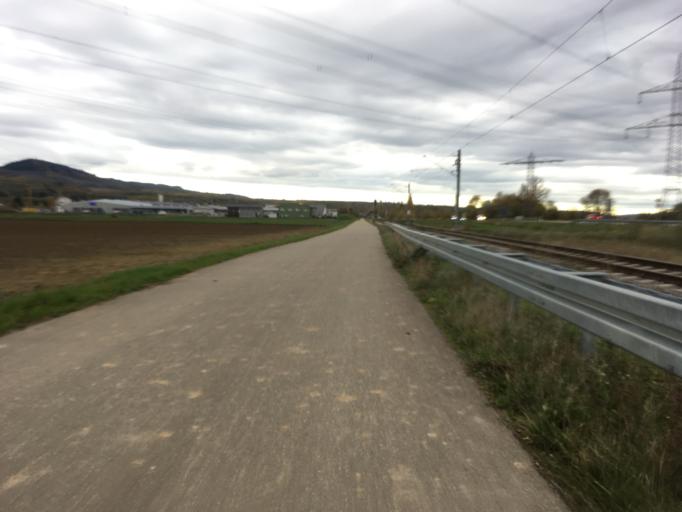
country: DE
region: Baden-Wuerttemberg
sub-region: Freiburg Region
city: Gottenheim
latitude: 48.0571
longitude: 7.7236
